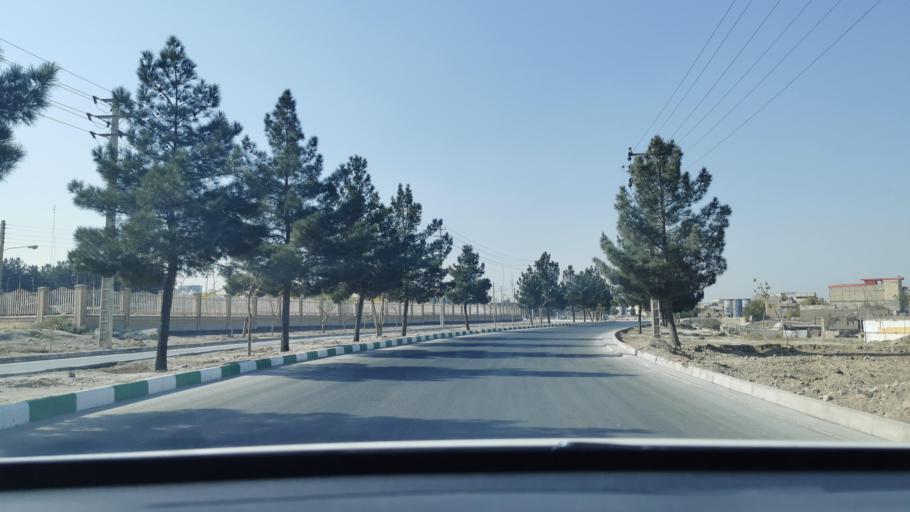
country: IR
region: Razavi Khorasan
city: Mashhad
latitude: 36.3481
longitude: 59.6036
